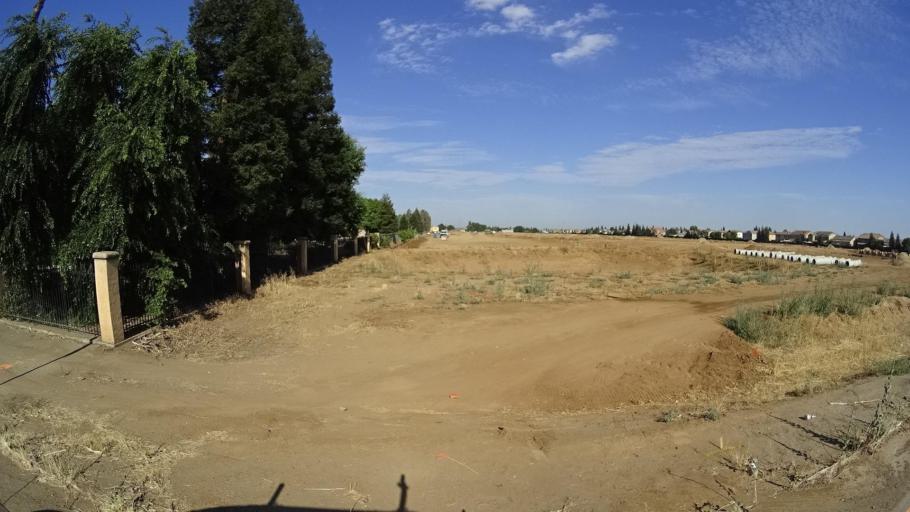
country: US
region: California
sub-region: Fresno County
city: Tarpey Village
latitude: 36.7740
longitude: -119.6641
